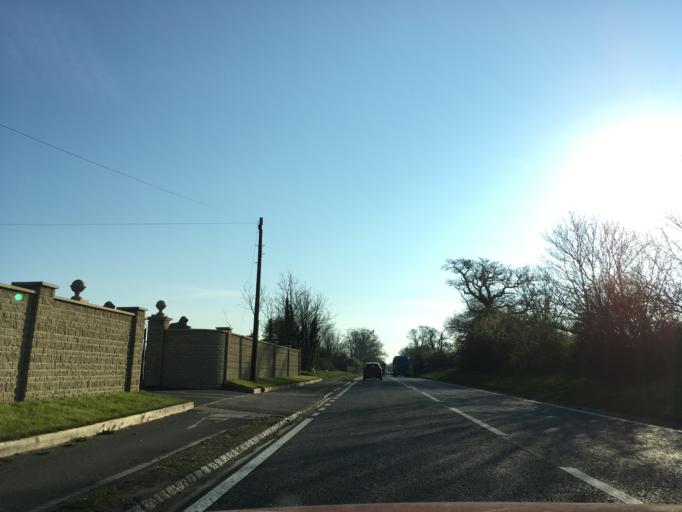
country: GB
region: England
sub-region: Oxfordshire
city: North Leigh
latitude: 51.7896
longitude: -1.4323
